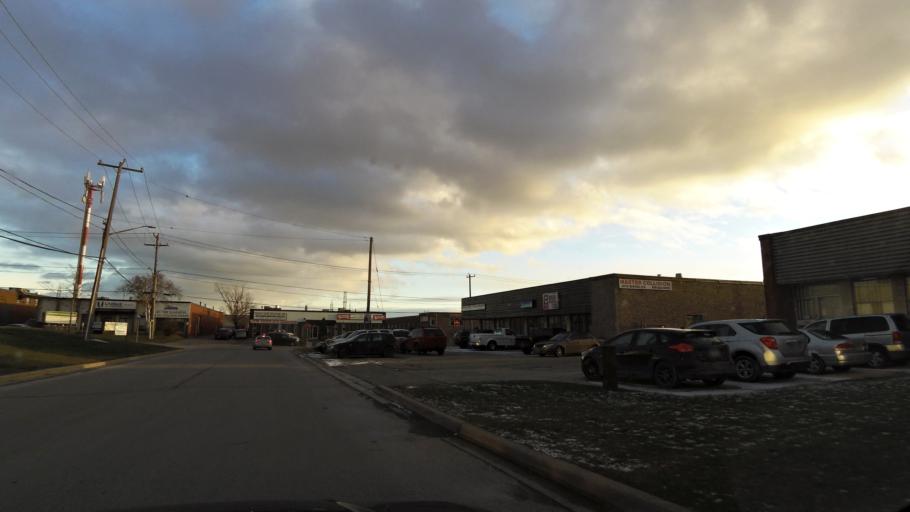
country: CA
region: Ontario
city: Etobicoke
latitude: 43.6315
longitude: -79.6223
